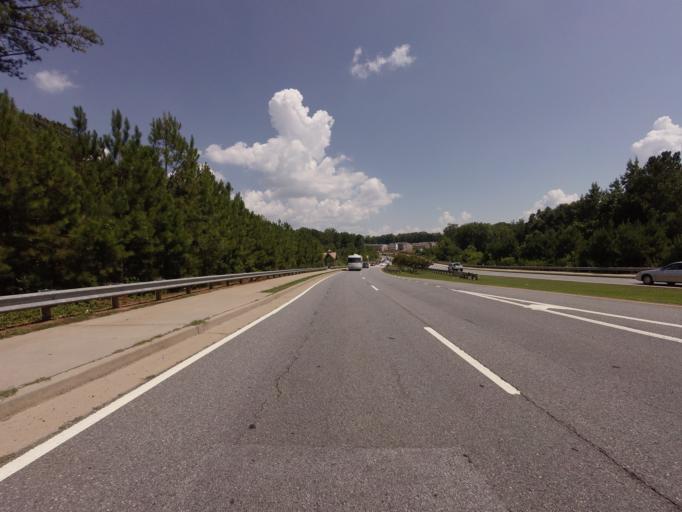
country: US
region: Georgia
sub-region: Fulton County
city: Johns Creek
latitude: 34.0282
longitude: -84.2033
